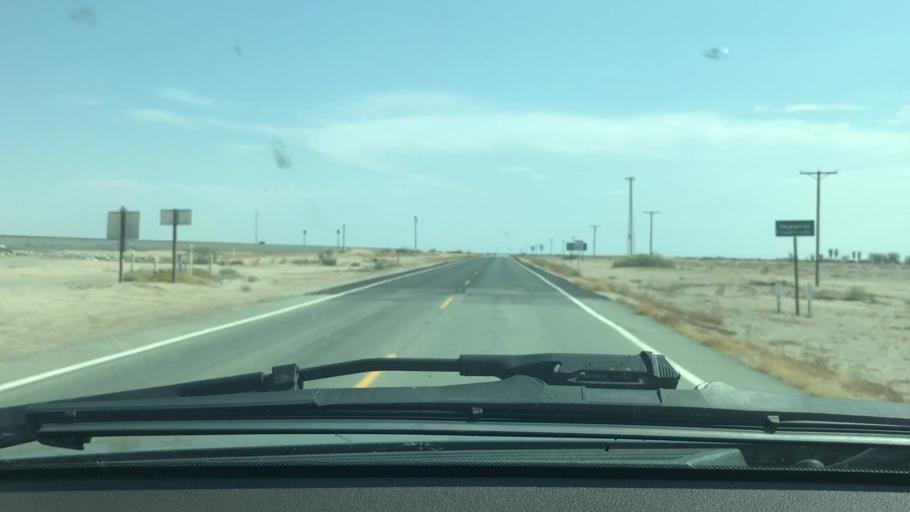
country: US
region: California
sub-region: Imperial County
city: Salton City
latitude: 33.4274
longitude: -115.8317
